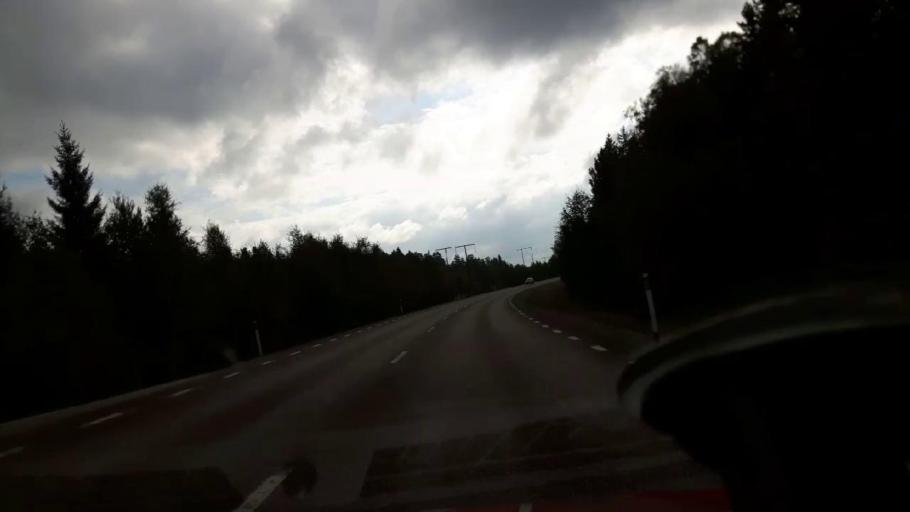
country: SE
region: Gaevleborg
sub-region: Soderhamns Kommun
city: Ljusne
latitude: 61.0957
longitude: 16.9544
